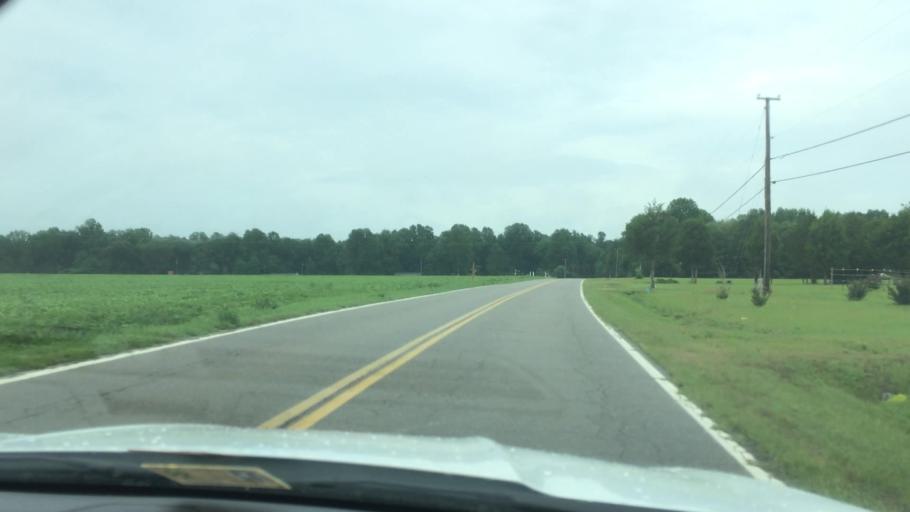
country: US
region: Virginia
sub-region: King William County
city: West Point
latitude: 37.5319
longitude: -76.7467
